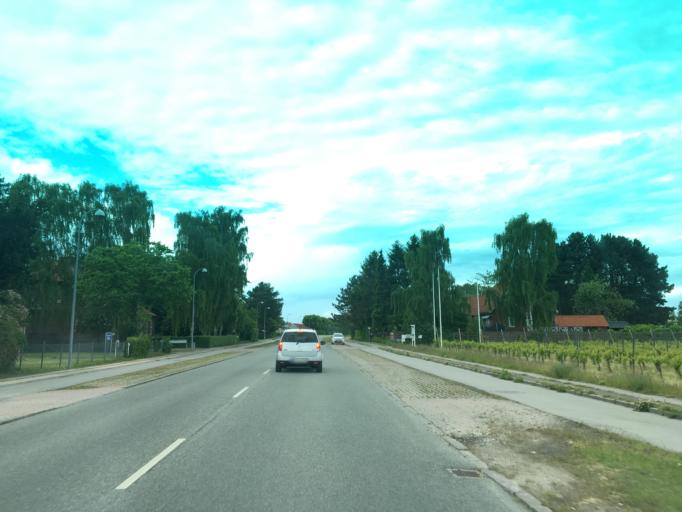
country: DK
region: Capital Region
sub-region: Hvidovre Kommune
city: Hvidovre
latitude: 55.6397
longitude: 12.4472
